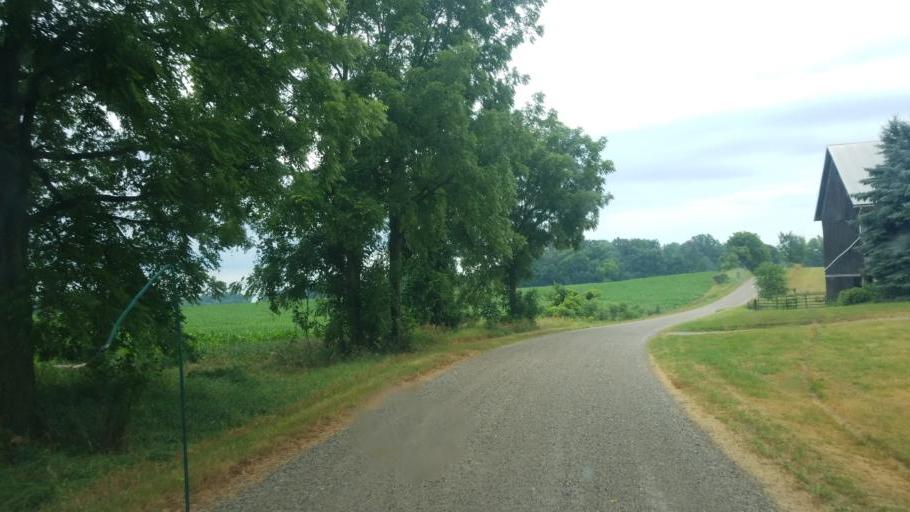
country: US
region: Indiana
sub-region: Steuben County
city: Hamilton
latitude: 41.5204
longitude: -84.9310
